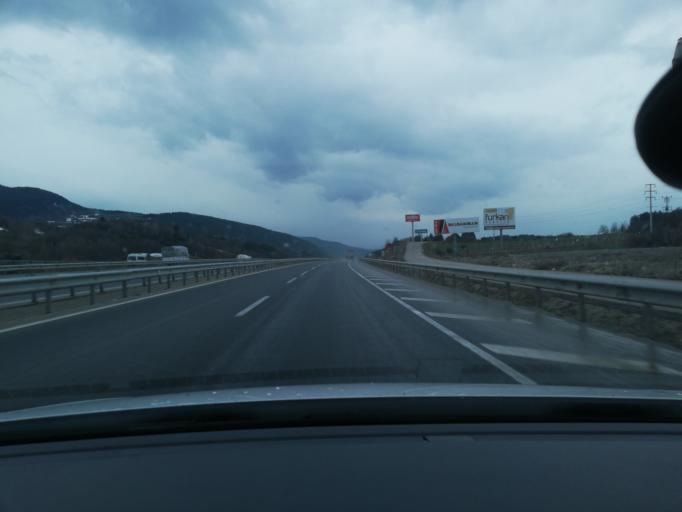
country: TR
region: Bolu
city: Yenicaga
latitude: 40.7536
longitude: 31.9085
